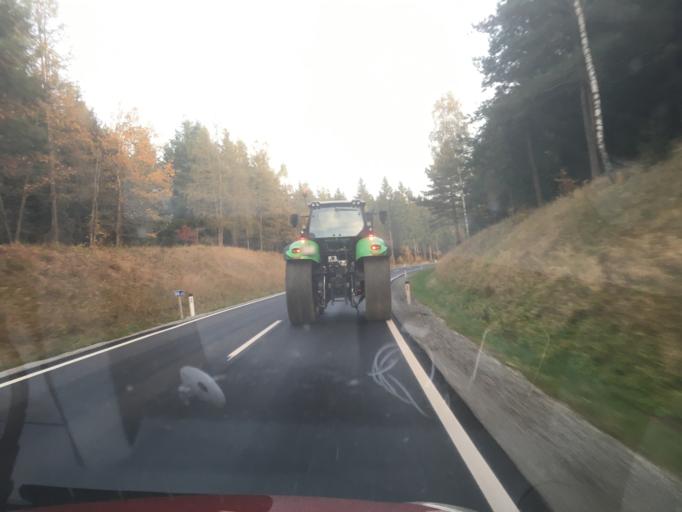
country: AT
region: Lower Austria
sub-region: Politischer Bezirk Zwettl
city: Langschlag
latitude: 48.5729
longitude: 14.9083
